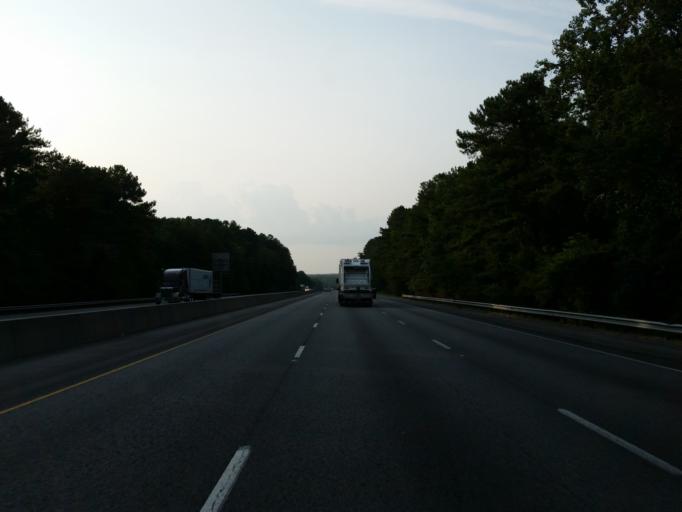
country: US
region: Georgia
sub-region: Bibb County
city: West Point
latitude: 32.8409
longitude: -83.7367
